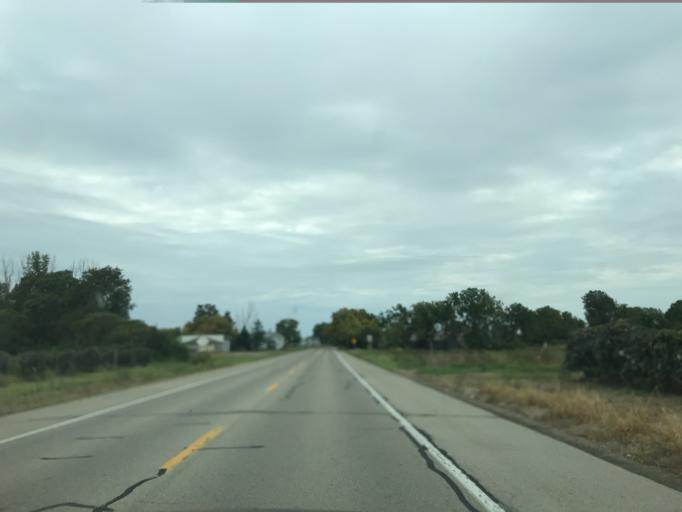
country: US
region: Pennsylvania
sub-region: Erie County
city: North East
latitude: 42.2406
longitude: -79.7659
